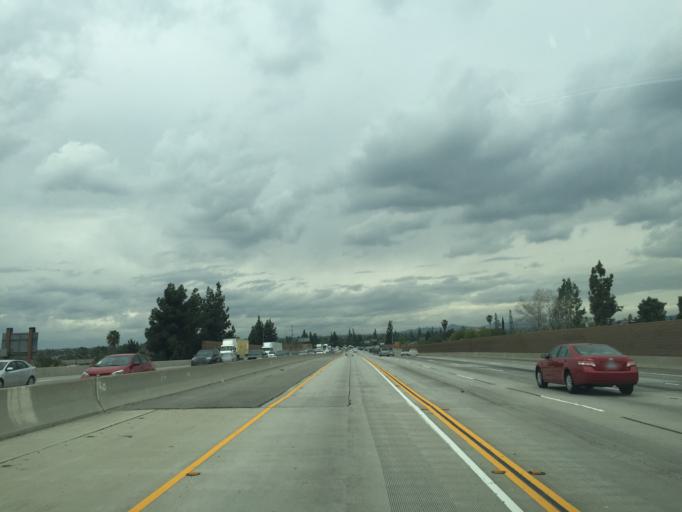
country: US
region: California
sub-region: Los Angeles County
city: Monrovia
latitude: 34.1355
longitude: -118.0004
